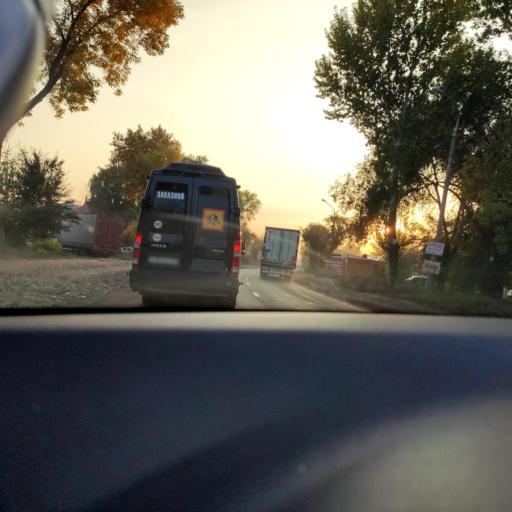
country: RU
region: Samara
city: Smyshlyayevka
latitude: 53.2308
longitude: 50.3044
